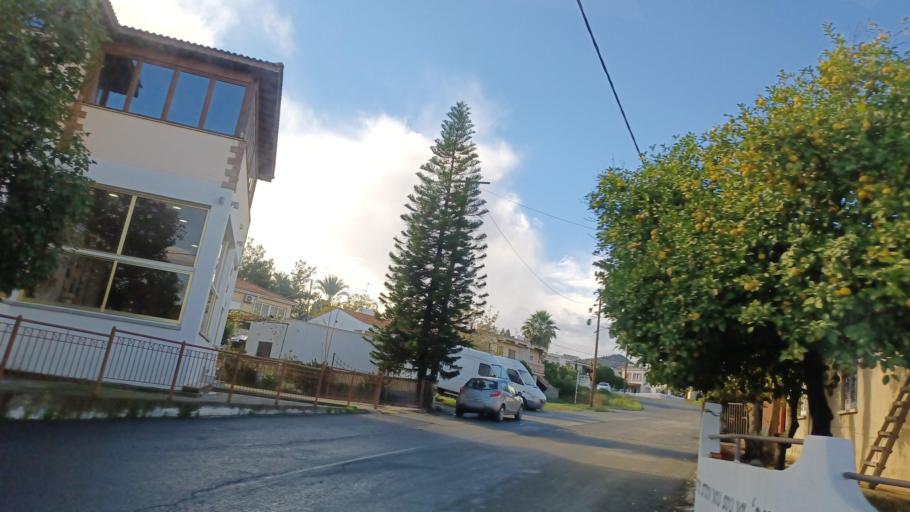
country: CY
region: Lefkosia
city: Lythrodontas
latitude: 34.9503
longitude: 33.2996
